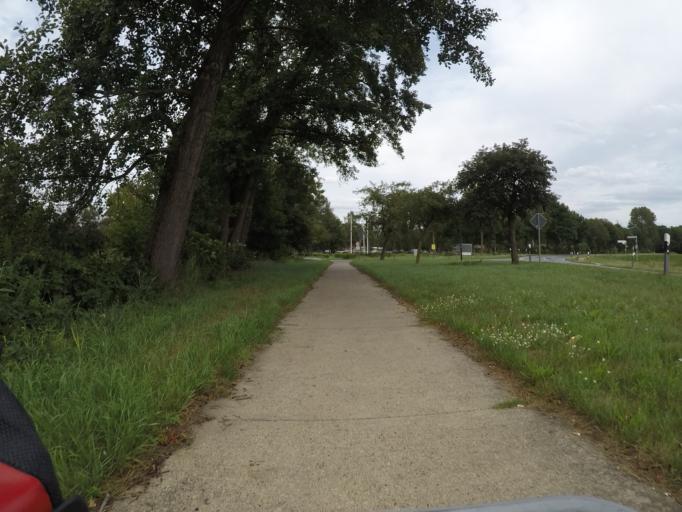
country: DE
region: Lower Saxony
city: Bardowick
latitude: 53.3034
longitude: 10.4017
